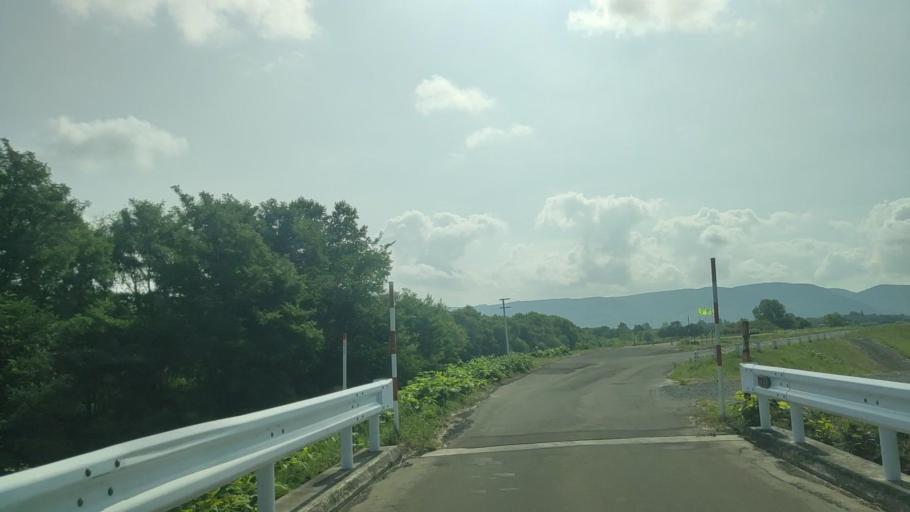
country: JP
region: Hokkaido
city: Shimo-furano
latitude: 43.3399
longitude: 142.3758
